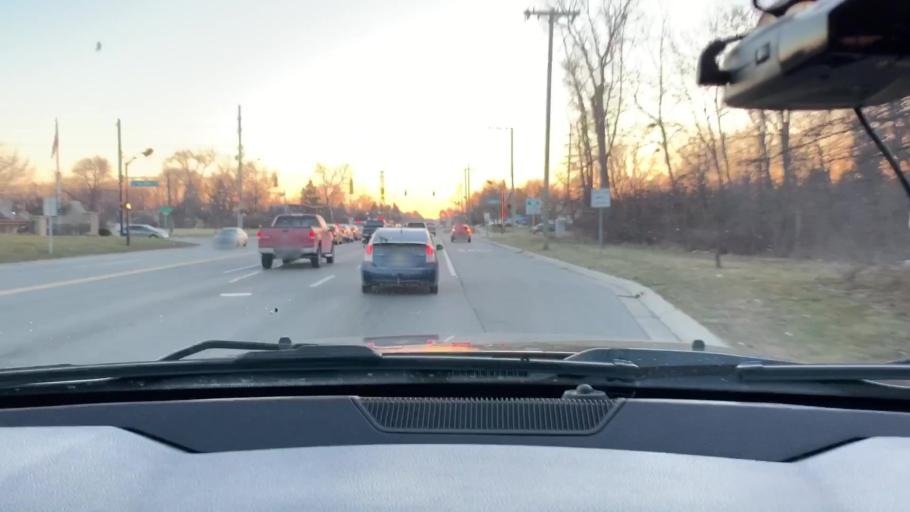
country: US
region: Michigan
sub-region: Wayne County
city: Flat Rock
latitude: 42.1245
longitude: -83.2754
